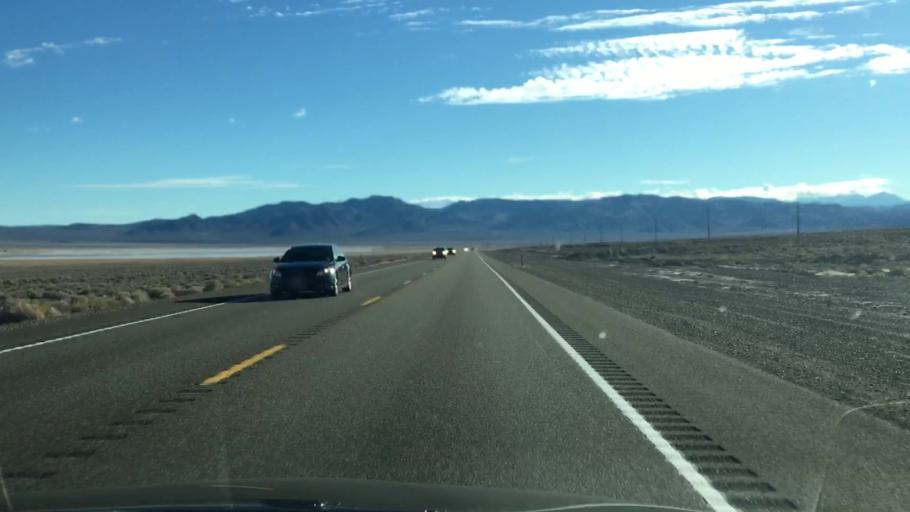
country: US
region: Nevada
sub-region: Mineral County
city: Hawthorne
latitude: 38.3201
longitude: -118.1027
